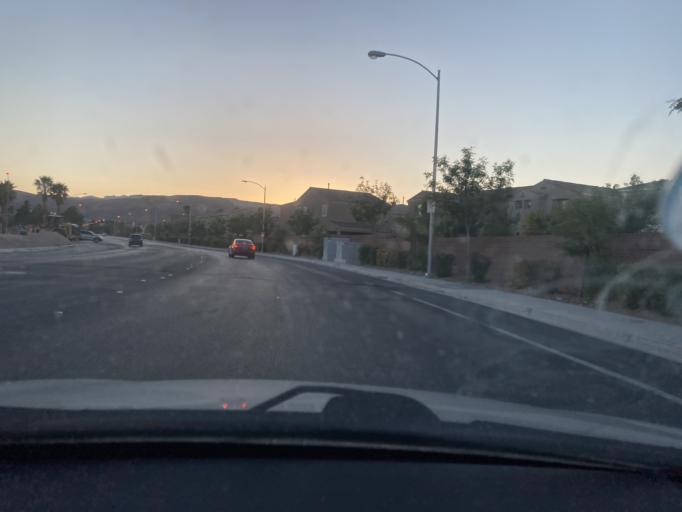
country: US
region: Nevada
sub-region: Clark County
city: Enterprise
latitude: 36.0627
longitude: -115.2872
